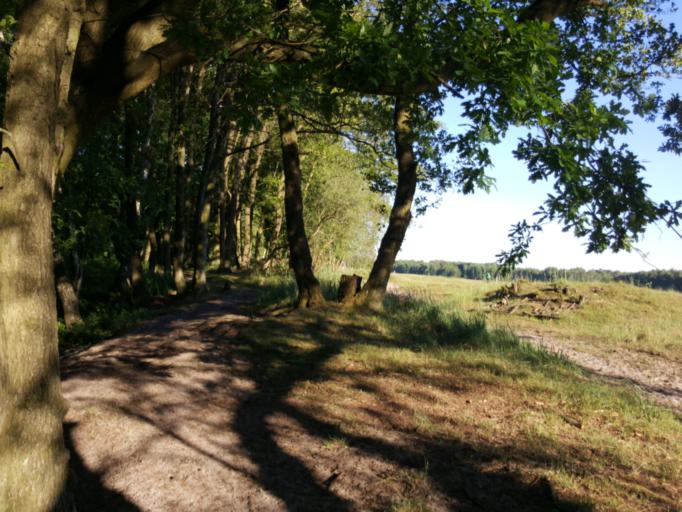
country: DE
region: Schleswig-Holstein
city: Oststeinbek
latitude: 53.5176
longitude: 10.1436
